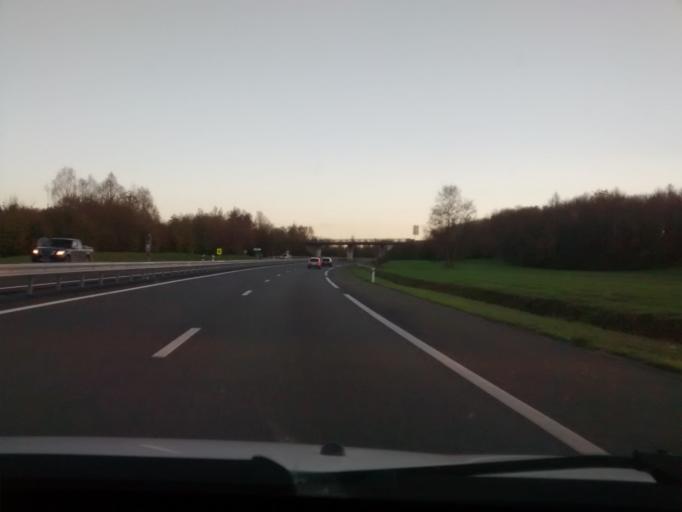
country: FR
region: Brittany
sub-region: Departement d'Ille-et-Vilaine
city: Saint-Pierre-de-Plesguen
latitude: 48.4300
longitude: -1.9150
